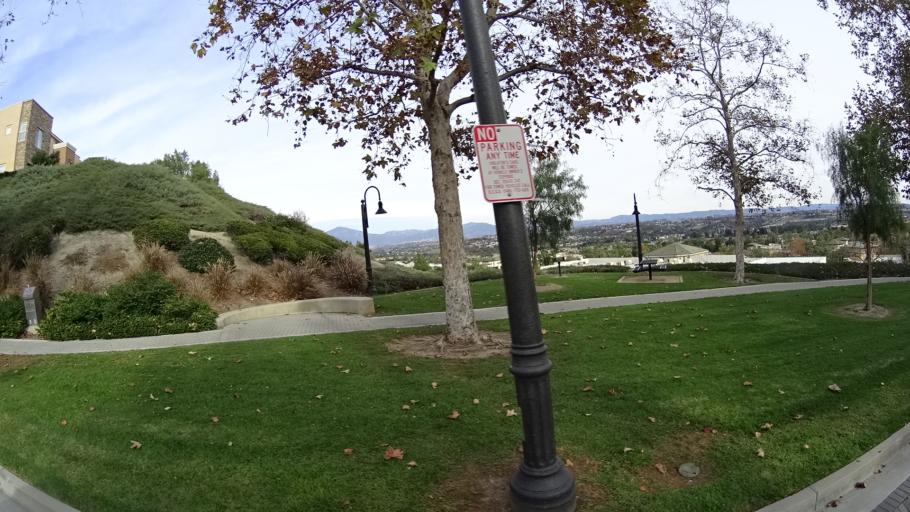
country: US
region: California
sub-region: Orange County
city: Aliso Viejo
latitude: 33.5765
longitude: -117.7287
